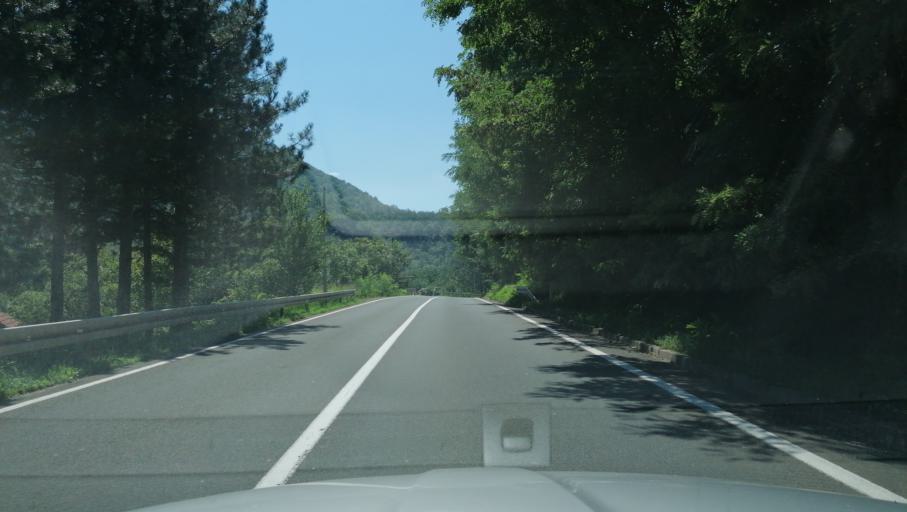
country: RS
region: Central Serbia
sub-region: Raski Okrug
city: Kraljevo
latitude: 43.6381
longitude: 20.5506
